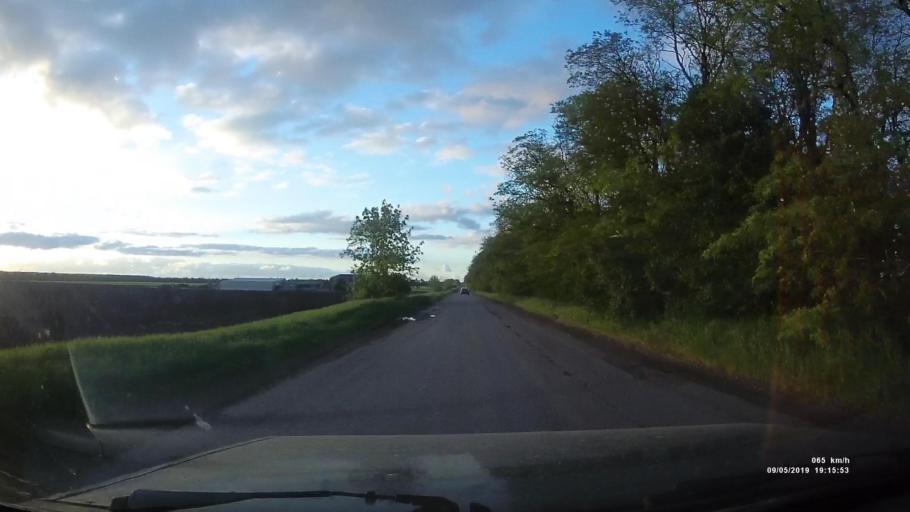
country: RU
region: Krasnodarskiy
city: Kanelovskaya
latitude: 46.7727
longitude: 39.2114
